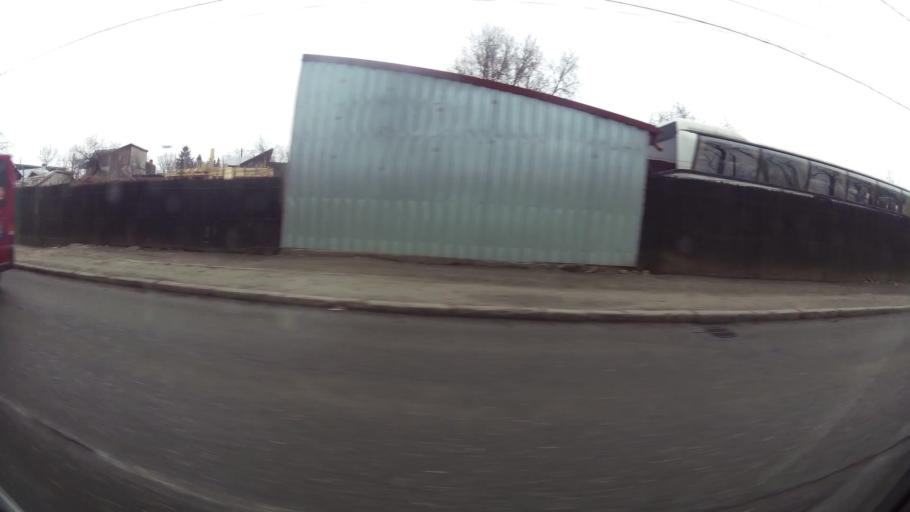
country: RO
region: Prahova
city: Ploiesti
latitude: 44.9443
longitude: 26.0464
